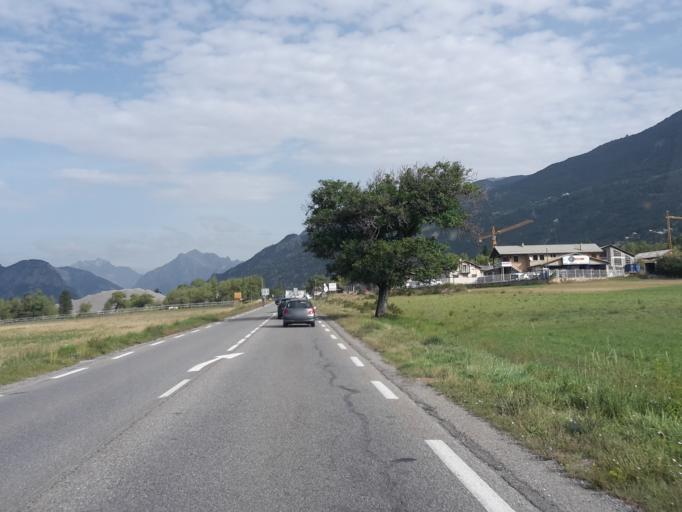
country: FR
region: Provence-Alpes-Cote d'Azur
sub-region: Departement des Hautes-Alpes
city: Guillestre
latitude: 44.6812
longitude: 6.6153
